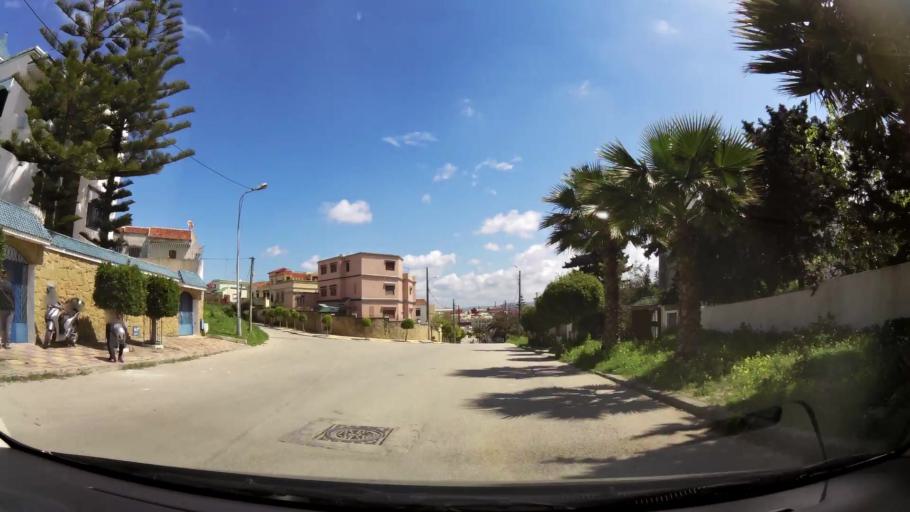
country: MA
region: Tanger-Tetouan
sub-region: Tanger-Assilah
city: Tangier
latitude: 35.7698
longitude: -5.8355
